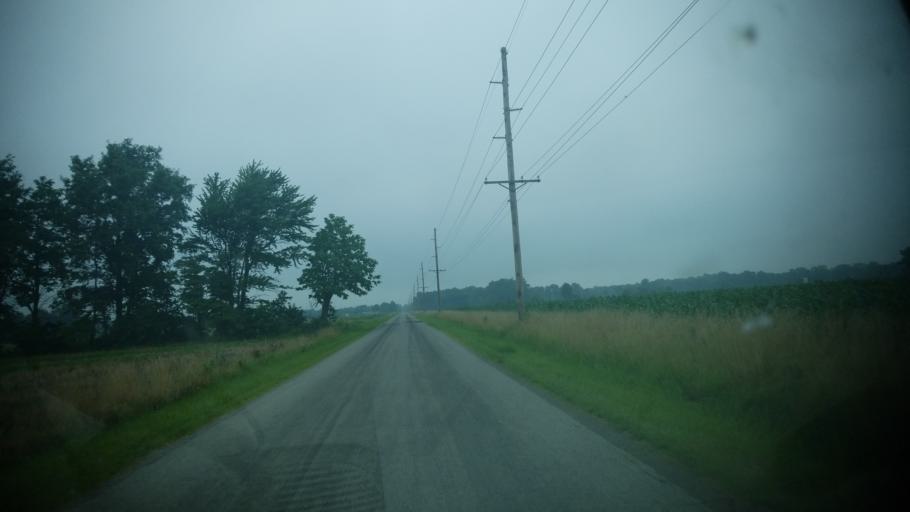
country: US
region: Illinois
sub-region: Clay County
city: Flora
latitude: 38.5476
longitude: -88.4020
